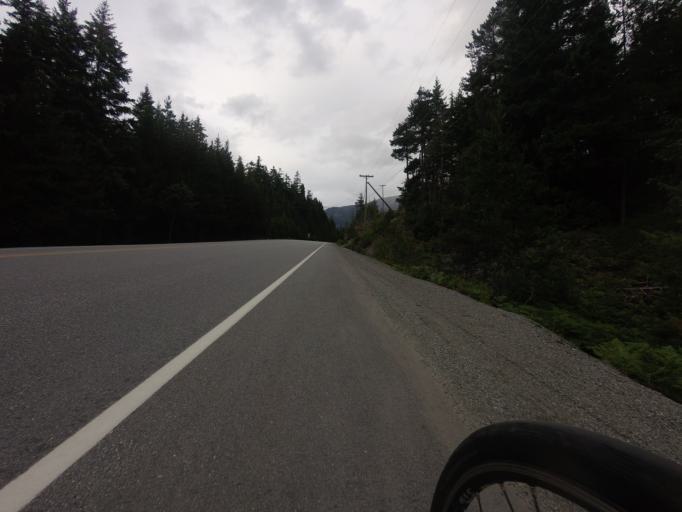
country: CA
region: British Columbia
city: Pemberton
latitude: 50.2230
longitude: -122.8774
